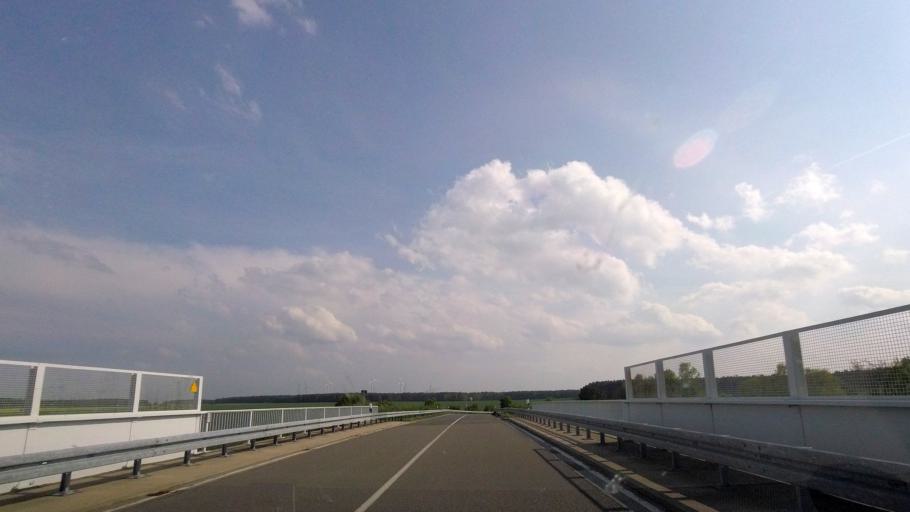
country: DE
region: Saxony-Anhalt
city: Zahna
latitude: 51.9417
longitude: 12.8351
